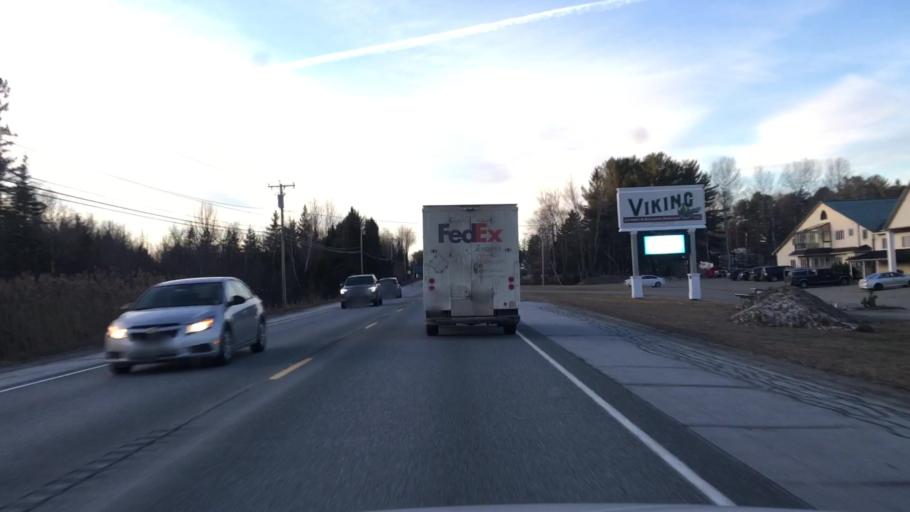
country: US
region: Maine
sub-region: Penobscot County
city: Holden
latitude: 44.7533
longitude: -68.6575
